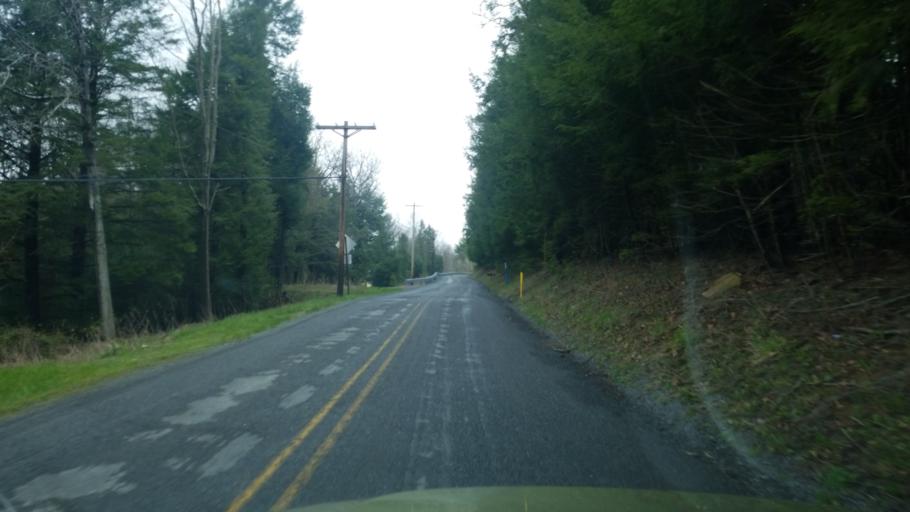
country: US
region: Pennsylvania
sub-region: Clearfield County
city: Clearfield
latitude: 41.0692
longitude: -78.4226
